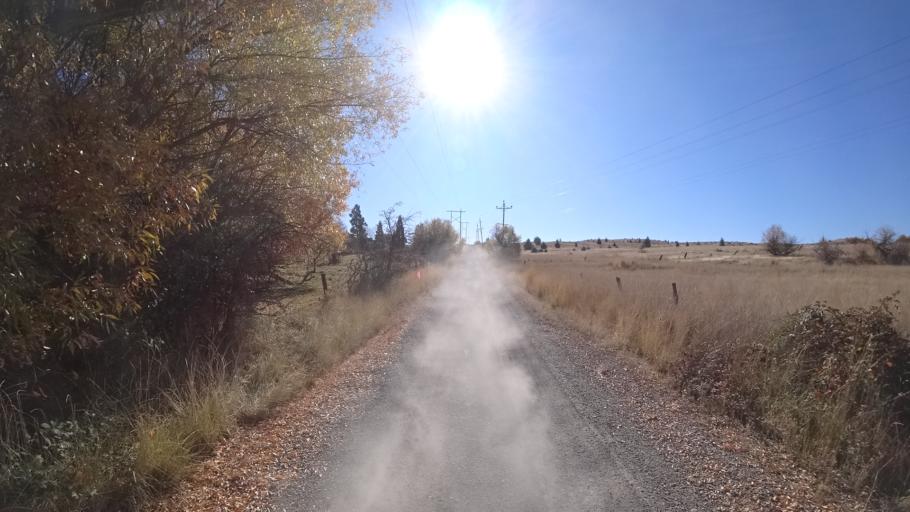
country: US
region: California
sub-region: Siskiyou County
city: Montague
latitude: 41.7870
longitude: -122.3589
